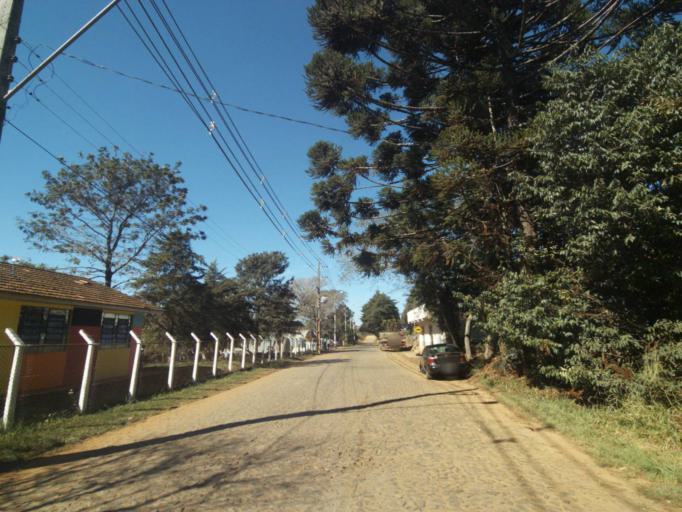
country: BR
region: Parana
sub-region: Reserva
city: Reserva
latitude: -24.6216
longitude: -50.6369
